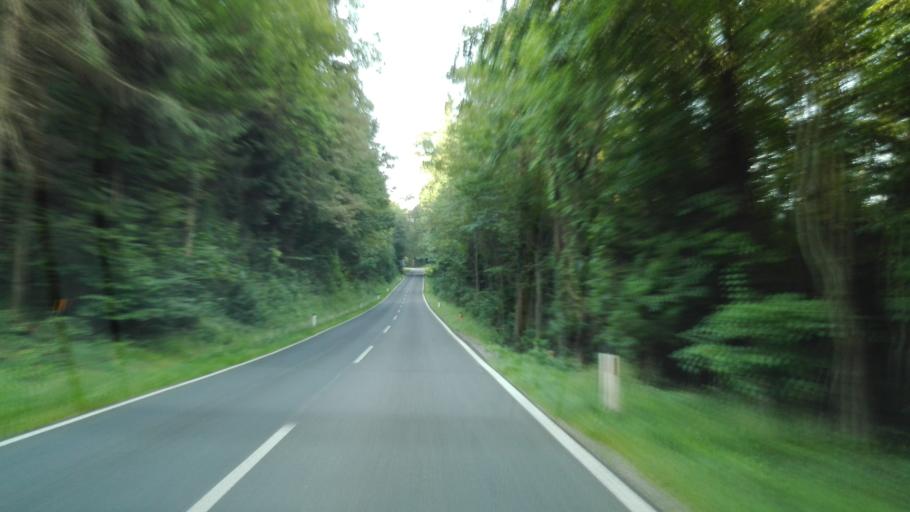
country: AT
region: Lower Austria
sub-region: Politischer Bezirk Lilienfeld
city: Rohrbach an der Goelsen
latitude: 48.0692
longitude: 15.7586
